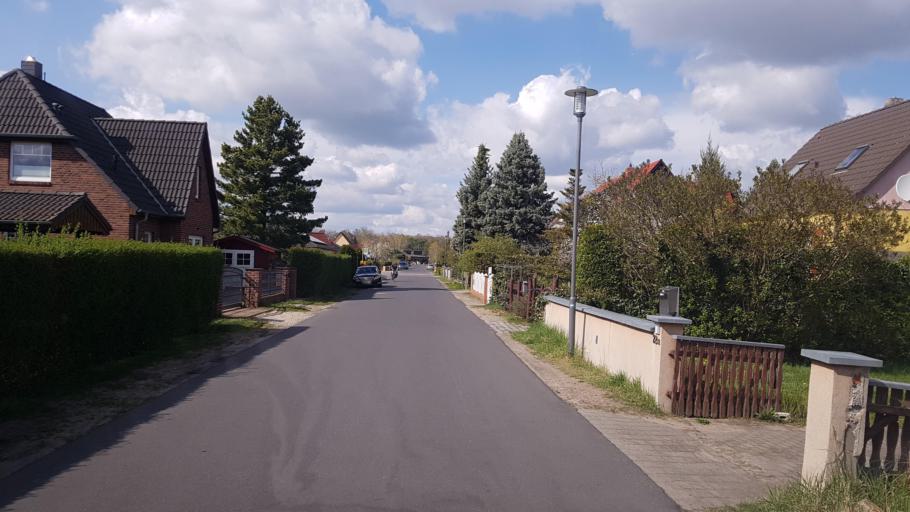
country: DE
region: Brandenburg
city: Luckenwalde
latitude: 52.0750
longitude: 13.1426
